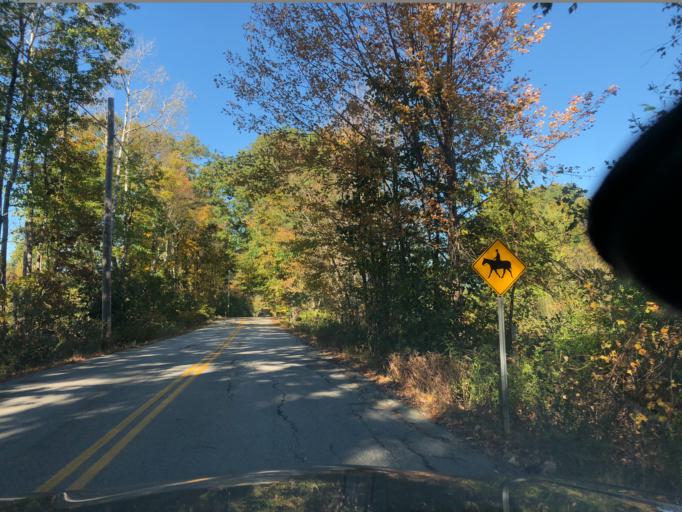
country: US
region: New Hampshire
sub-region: Strafford County
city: Lee
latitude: 43.1150
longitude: -70.9695
